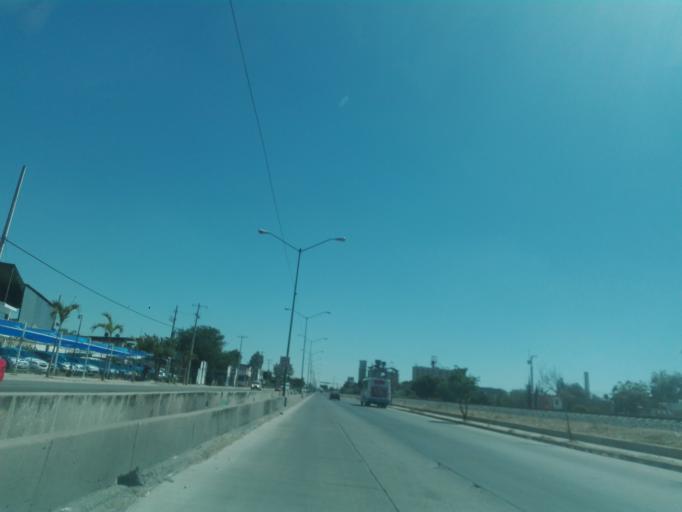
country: MX
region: Guanajuato
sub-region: Leon
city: San Jose de Duran (Los Troncoso)
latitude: 21.0879
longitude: -101.6724
